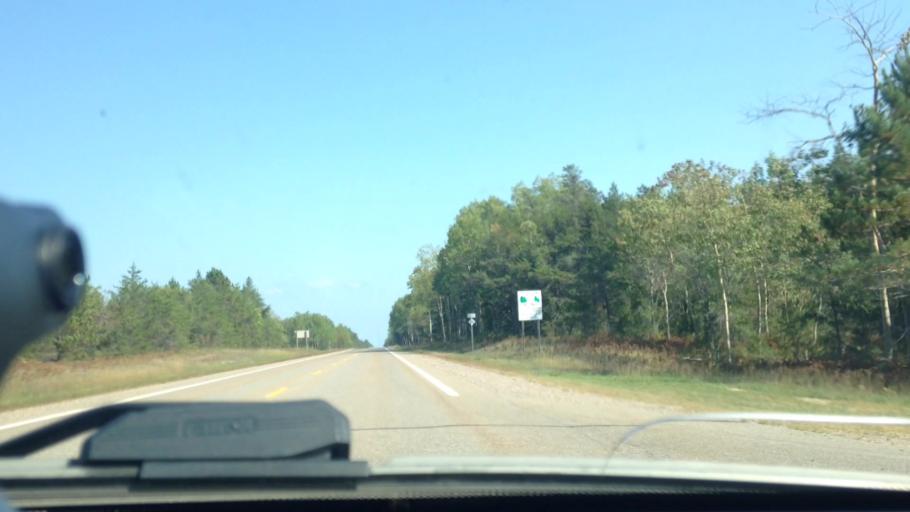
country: US
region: Michigan
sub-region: Mackinac County
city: Saint Ignace
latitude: 46.3584
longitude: -84.8630
